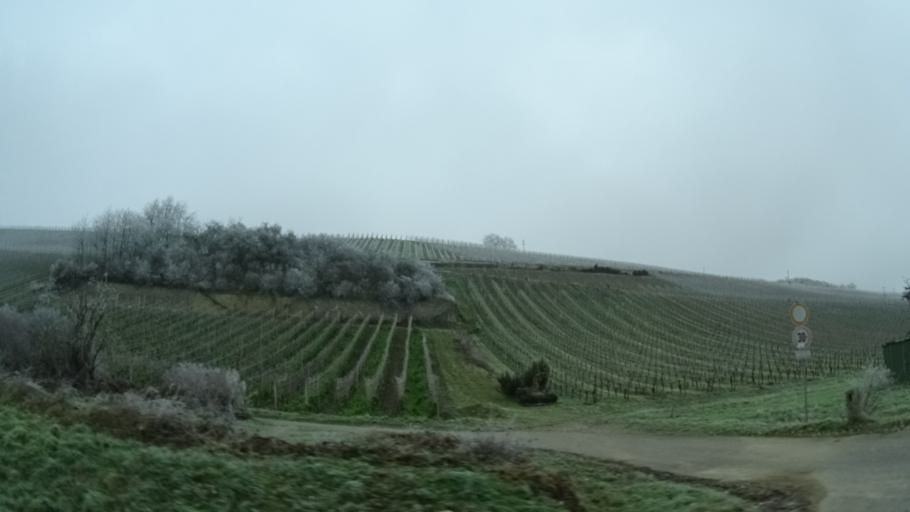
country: DE
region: Bavaria
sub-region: Regierungsbezirk Unterfranken
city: Frickenhausen
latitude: 49.6696
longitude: 10.1144
